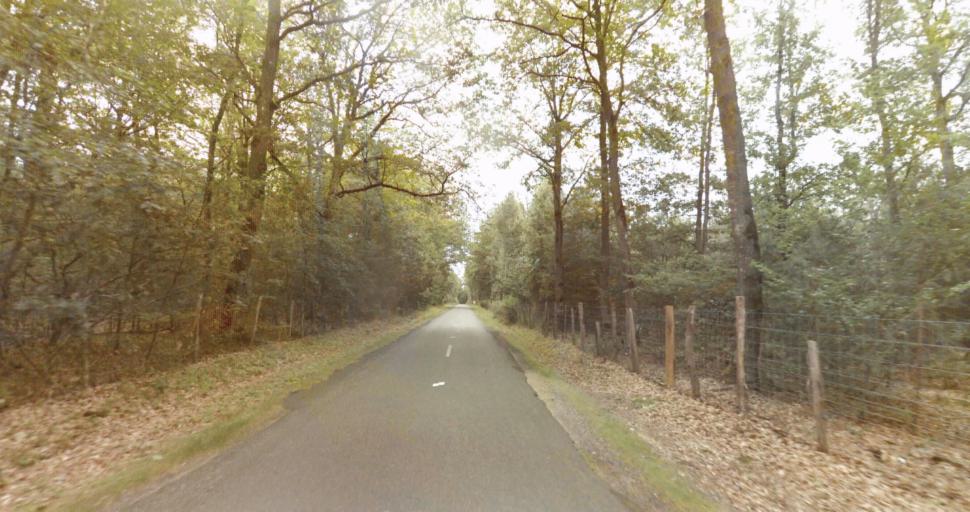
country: FR
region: Haute-Normandie
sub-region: Departement de l'Eure
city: Croth
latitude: 48.8600
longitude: 1.3580
